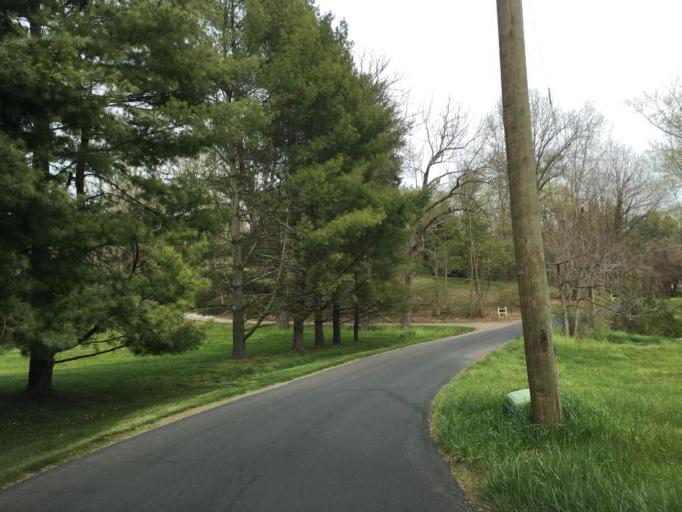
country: US
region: Maryland
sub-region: Baltimore County
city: Hunt Valley
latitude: 39.5692
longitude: -76.6216
